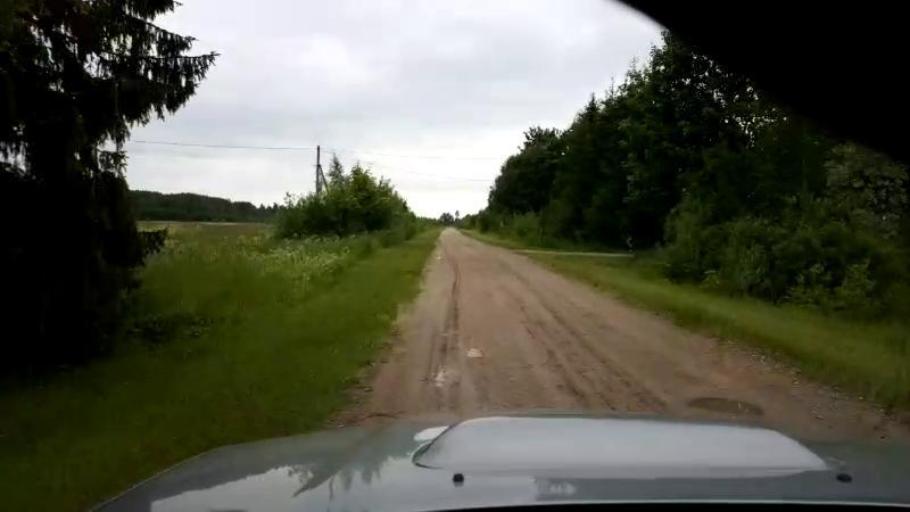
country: EE
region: Paernumaa
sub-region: Halinga vald
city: Parnu-Jaagupi
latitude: 58.5564
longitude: 24.5751
